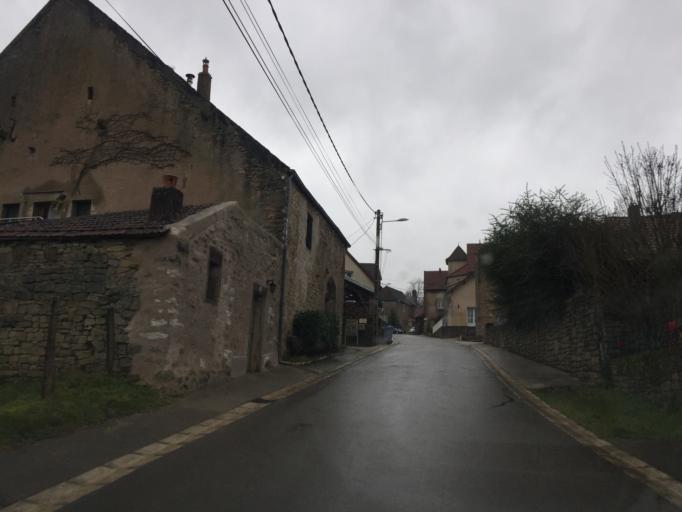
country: FR
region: Franche-Comte
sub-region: Departement du Jura
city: Dole
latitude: 47.1567
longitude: 5.5146
